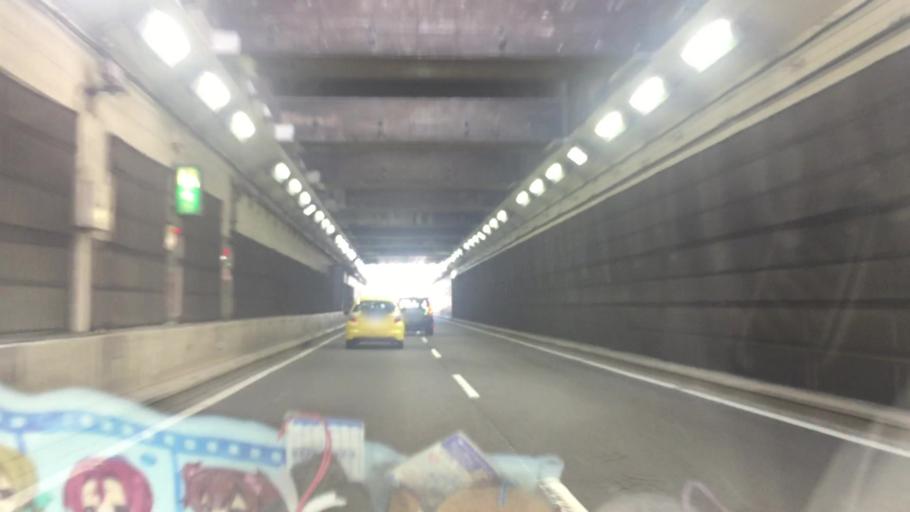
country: JP
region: Kanagawa
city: Yokohama
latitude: 35.4699
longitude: 139.6134
